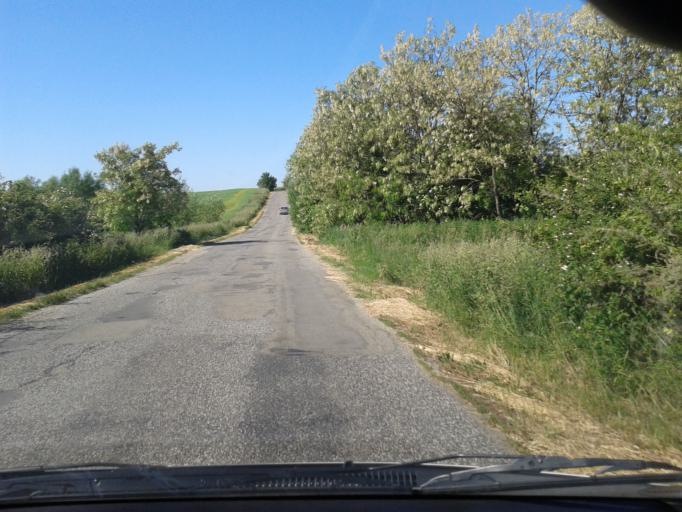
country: SK
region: Nitriansky
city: Levice
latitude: 48.1226
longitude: 18.4481
